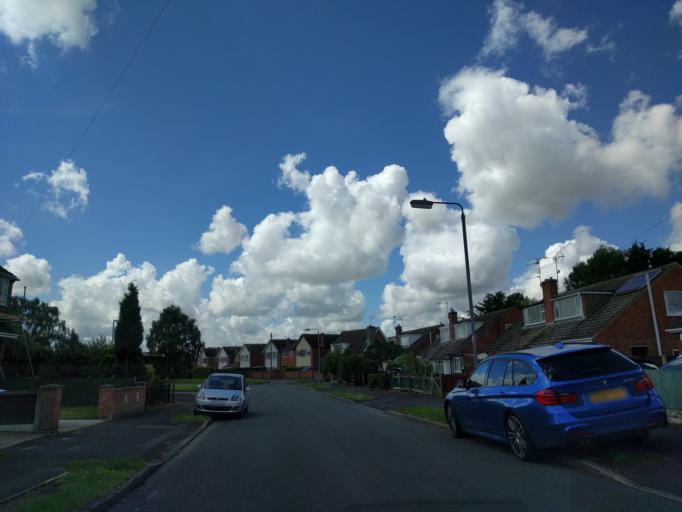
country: GB
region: England
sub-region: Nottinghamshire
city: Newark on Trent
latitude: 53.0623
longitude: -0.8286
